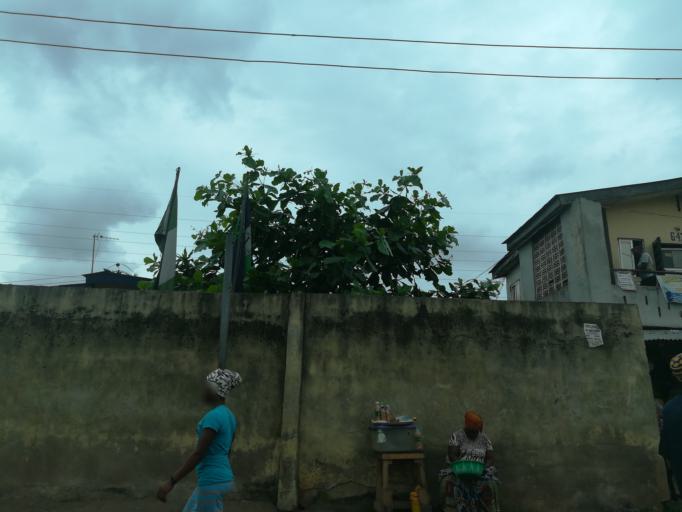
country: NG
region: Lagos
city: Ojota
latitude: 6.6070
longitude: 3.3978
